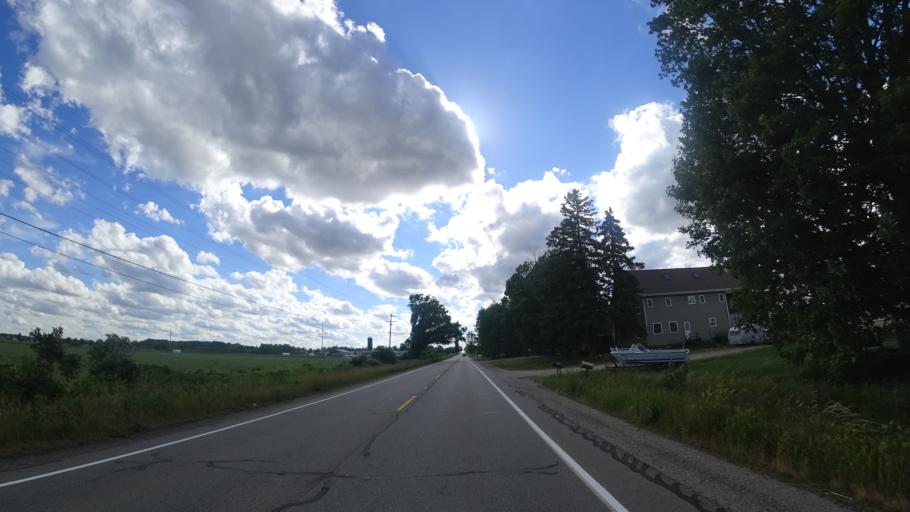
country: US
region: Michigan
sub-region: Ionia County
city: Portland
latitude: 42.8716
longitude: -84.9225
